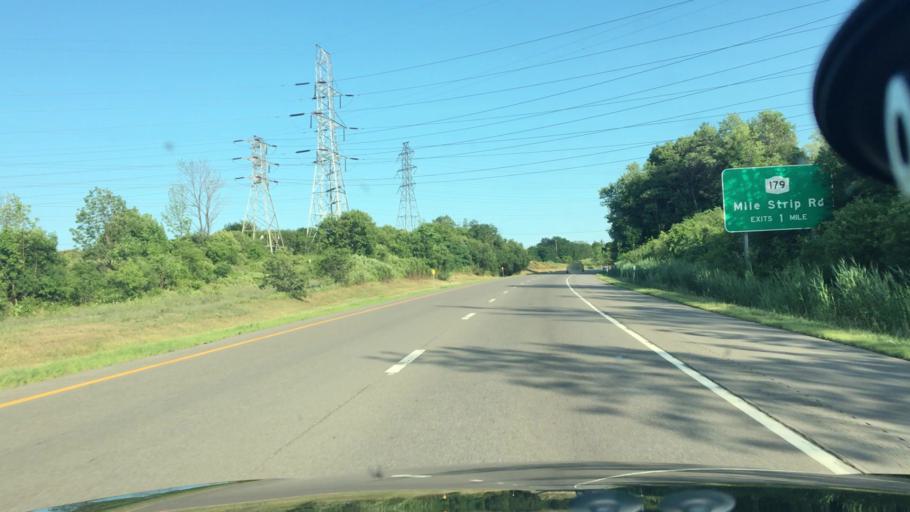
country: US
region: New York
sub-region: Erie County
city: Blasdell
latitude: 42.8074
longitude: -78.7835
